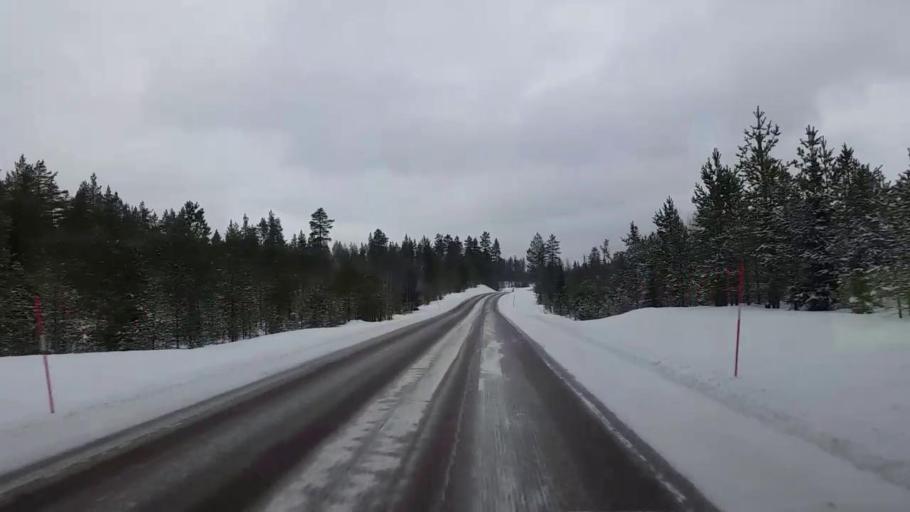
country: SE
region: Jaemtland
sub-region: Bergs Kommun
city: Hoverberg
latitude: 62.4269
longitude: 14.6003
